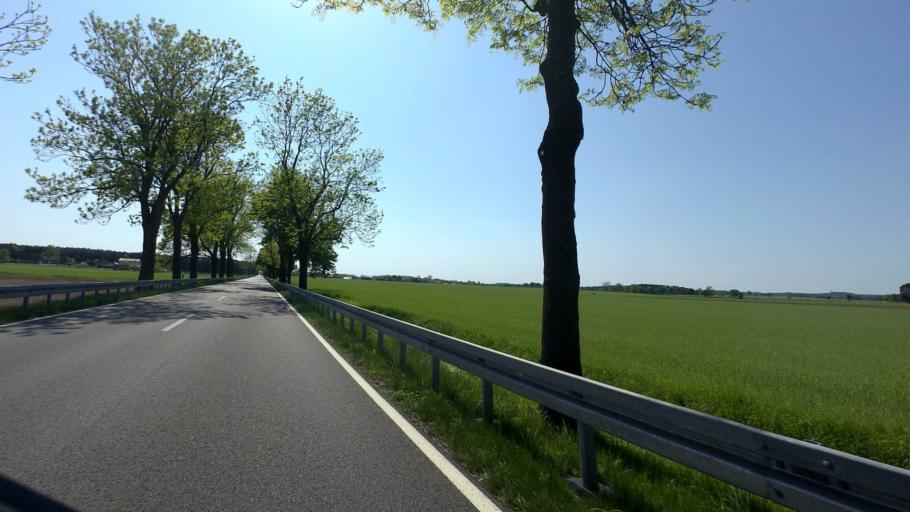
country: DE
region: Brandenburg
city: Neu Zauche
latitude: 52.0340
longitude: 14.0986
